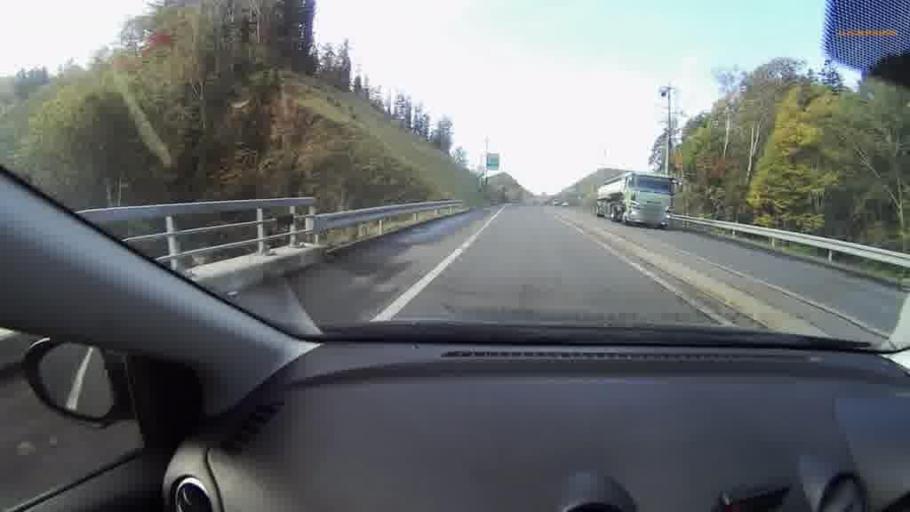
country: JP
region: Hokkaido
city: Kushiro
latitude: 43.0057
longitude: 144.5066
